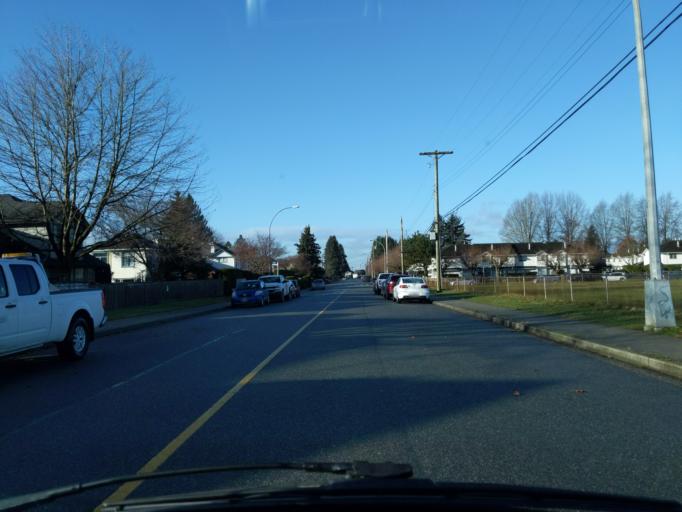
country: CA
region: British Columbia
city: Pitt Meadows
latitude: 49.2191
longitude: -122.6923
